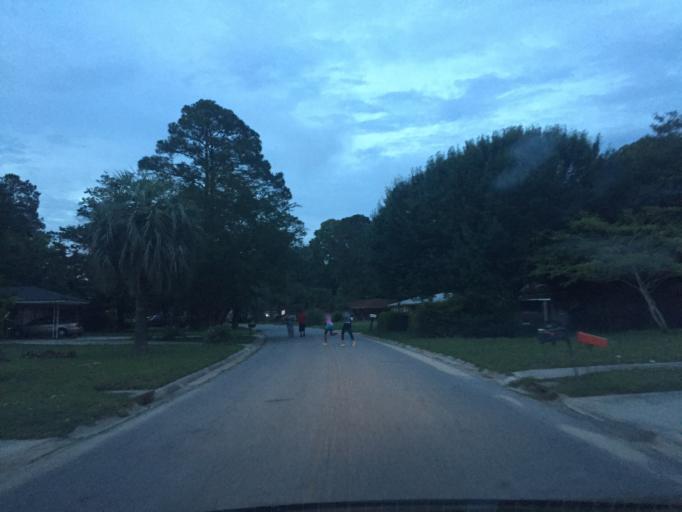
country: US
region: Georgia
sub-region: Chatham County
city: Montgomery
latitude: 31.9888
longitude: -81.1235
